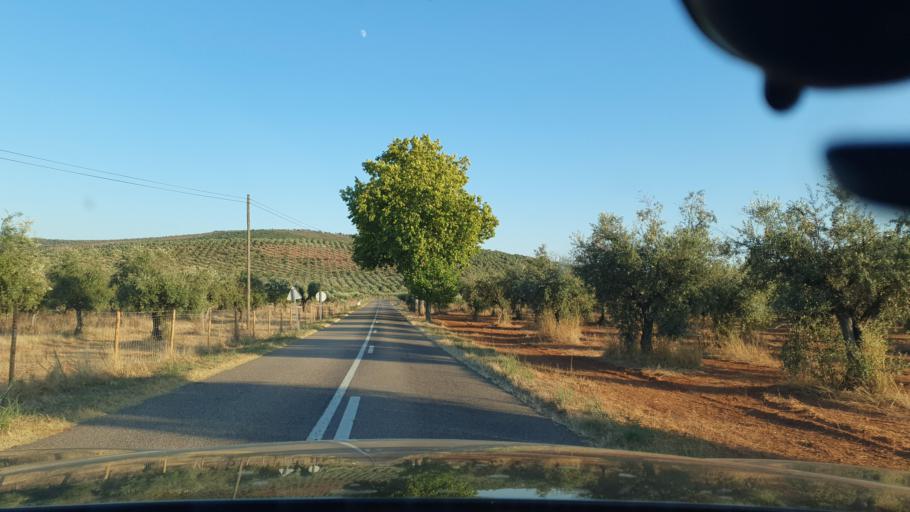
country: PT
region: Evora
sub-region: Estremoz
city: Estremoz
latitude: 38.9316
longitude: -7.6672
